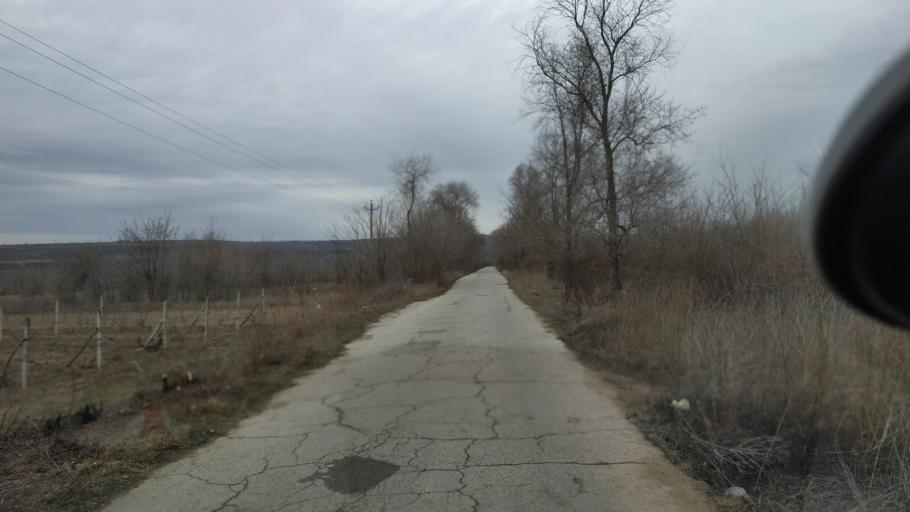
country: MD
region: Telenesti
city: Cocieri
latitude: 47.3267
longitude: 29.0944
